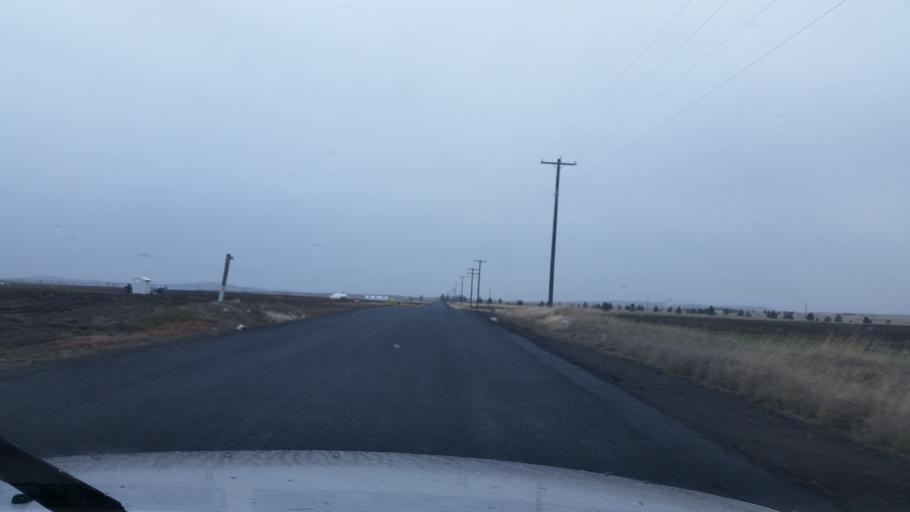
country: US
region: Washington
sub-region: Spokane County
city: Medical Lake
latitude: 47.6144
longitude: -117.7554
